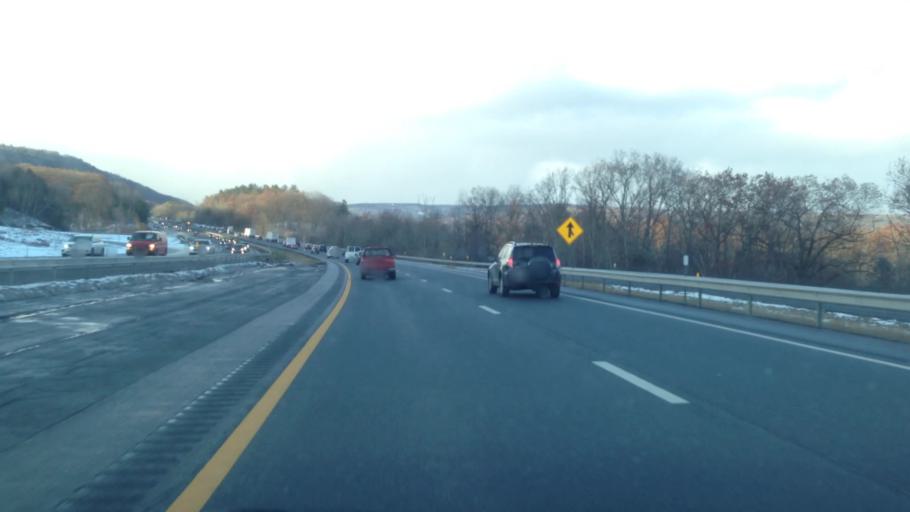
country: US
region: New York
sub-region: Schenectady County
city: Scotia
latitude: 42.8391
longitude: -74.0134
